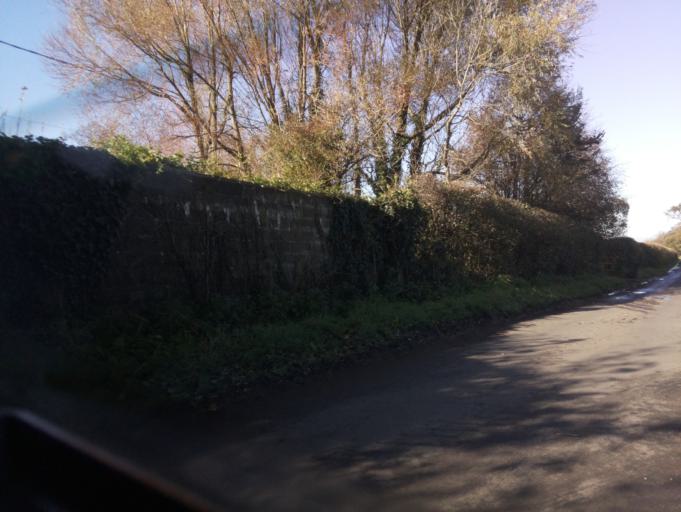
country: GB
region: England
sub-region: Dorset
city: Sherborne
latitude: 50.8597
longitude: -2.5122
